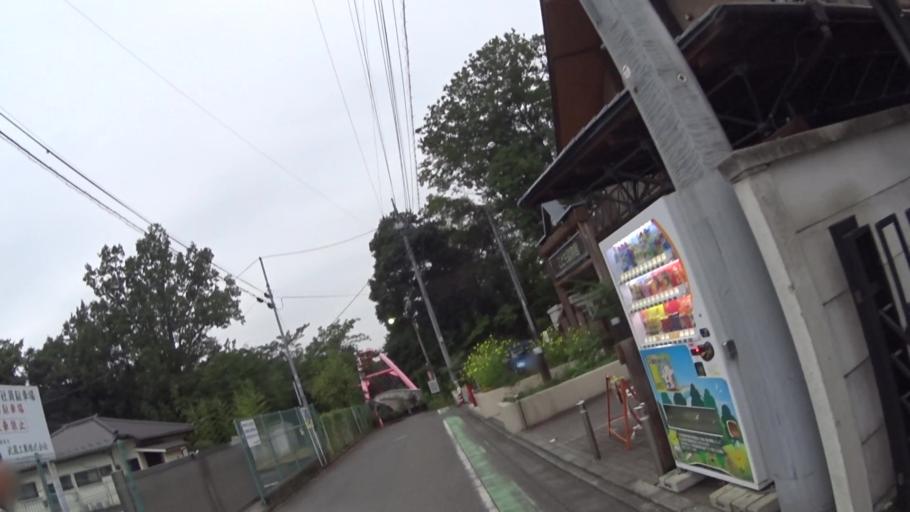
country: JP
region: Saitama
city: Hanno
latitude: 35.8538
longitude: 139.3115
